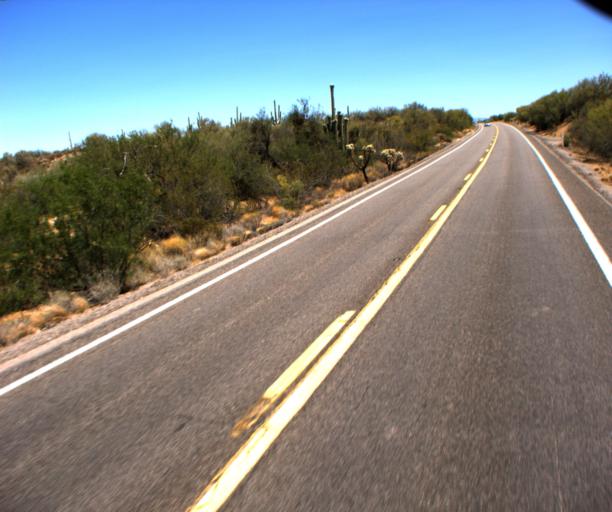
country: US
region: Arizona
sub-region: Pima County
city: Marana
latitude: 32.7721
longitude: -111.1598
